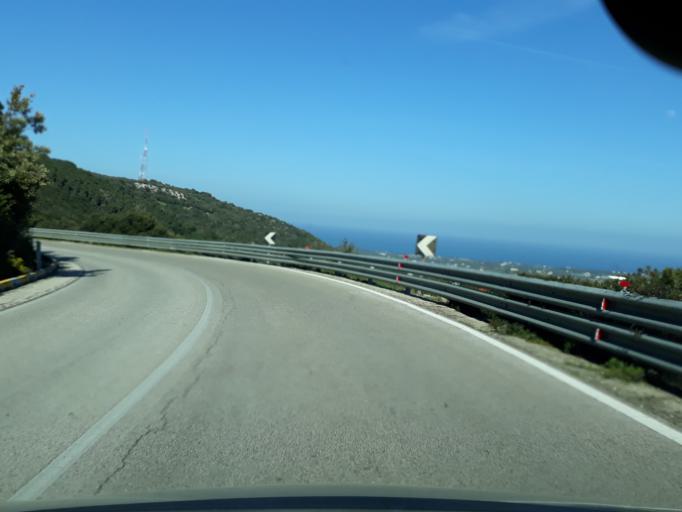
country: IT
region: Apulia
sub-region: Provincia di Bari
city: Cozzana
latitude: 40.8877
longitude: 17.2773
